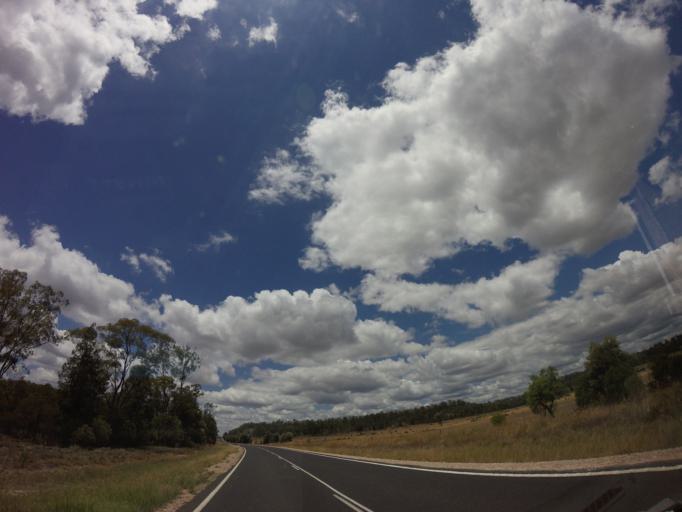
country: AU
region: Queensland
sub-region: Goondiwindi
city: Goondiwindi
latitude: -28.0376
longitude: 150.8096
